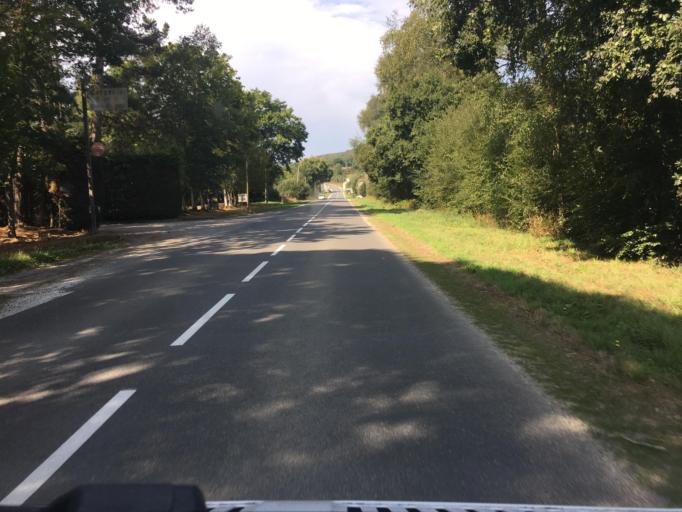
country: FR
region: Brittany
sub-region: Departement des Cotes-d'Armor
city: Gouarec
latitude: 48.2143
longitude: -3.1222
